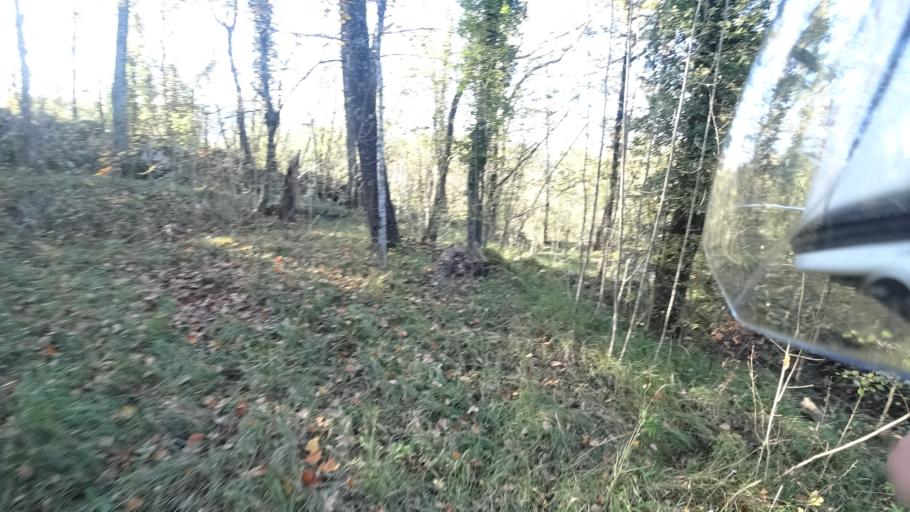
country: HR
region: Primorsko-Goranska
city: Matulji
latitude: 45.4035
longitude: 14.2873
